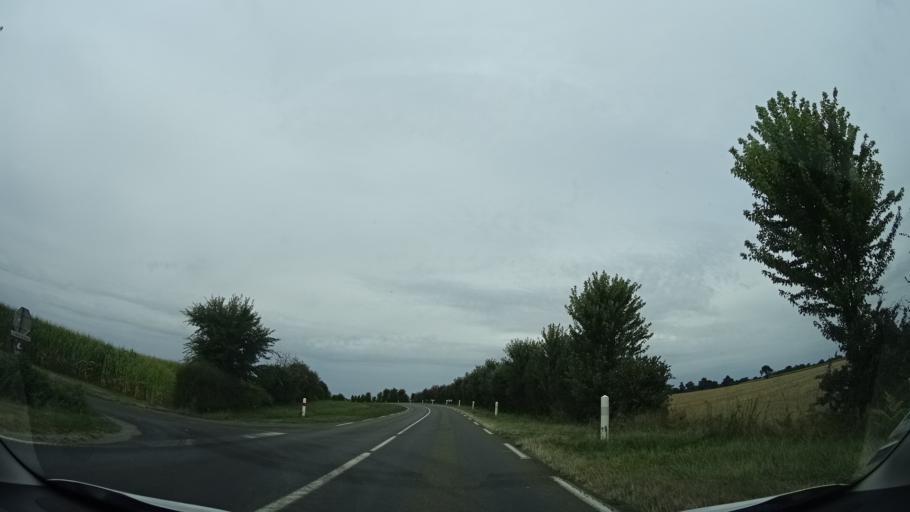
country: FR
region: Pays de la Loire
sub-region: Departement de la Mayenne
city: Meslay-du-Maine
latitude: 47.9452
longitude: -0.5247
